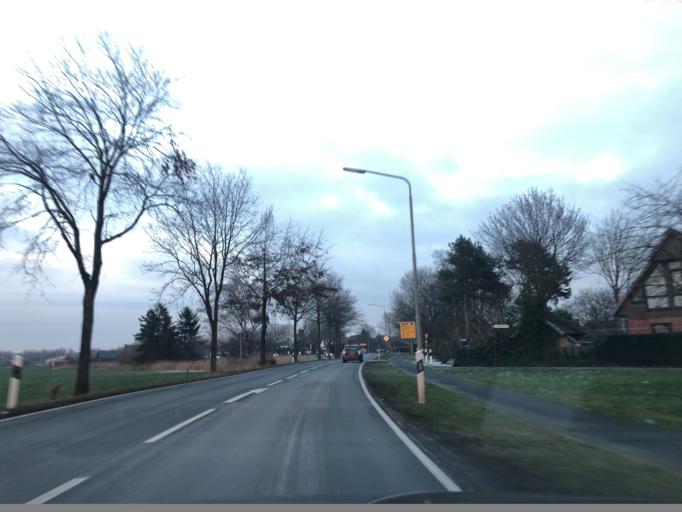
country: DE
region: Lower Saxony
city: Lemwerder
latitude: 53.1495
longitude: 8.6051
